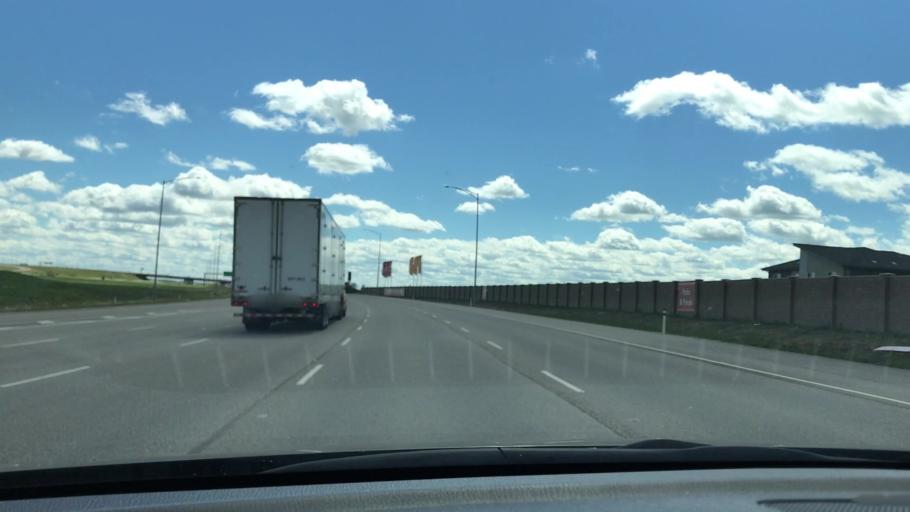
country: CA
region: Alberta
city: Beaumont
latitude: 53.4078
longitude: -113.5050
